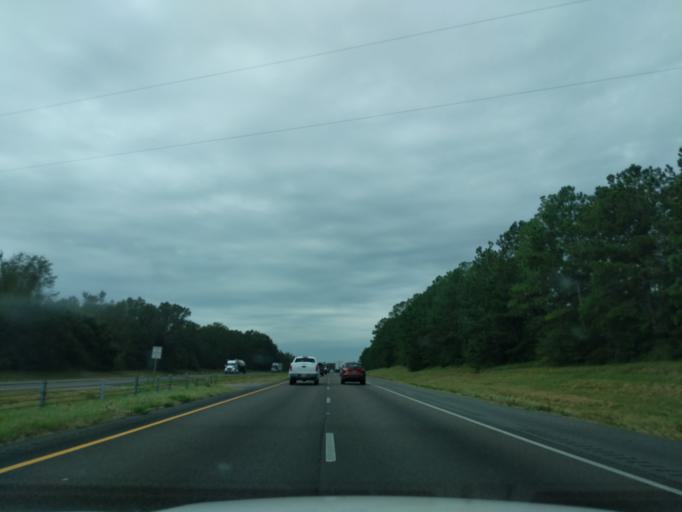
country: US
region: Alabama
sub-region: Mobile County
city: Grand Bay
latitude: 30.5110
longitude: -88.2865
